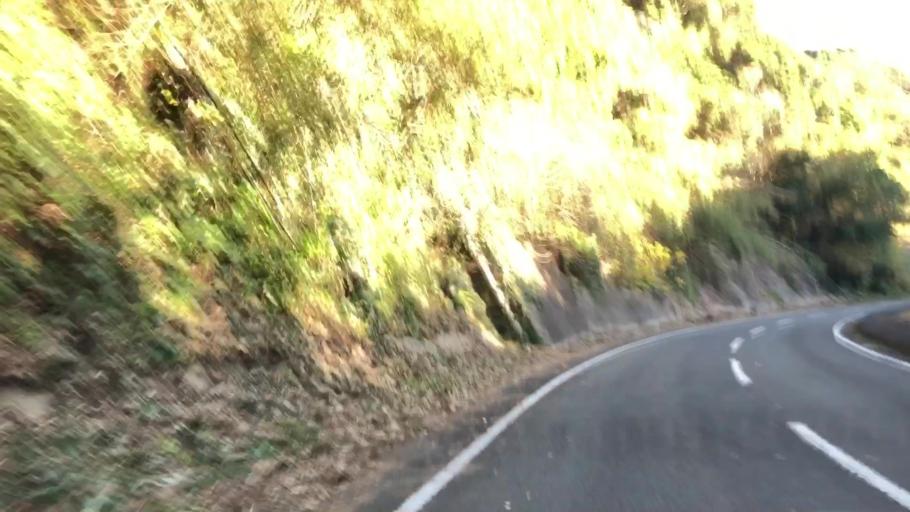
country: JP
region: Nagasaki
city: Sasebo
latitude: 33.0279
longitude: 129.6637
